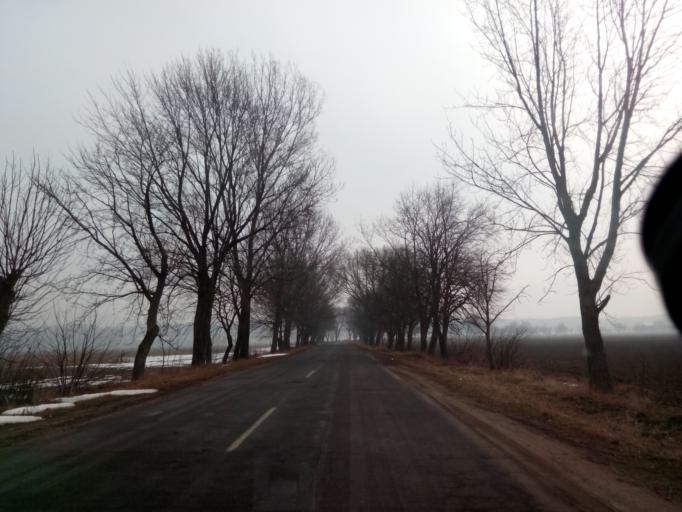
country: HU
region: Borsod-Abauj-Zemplen
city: Gonc
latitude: 48.4932
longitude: 21.2451
